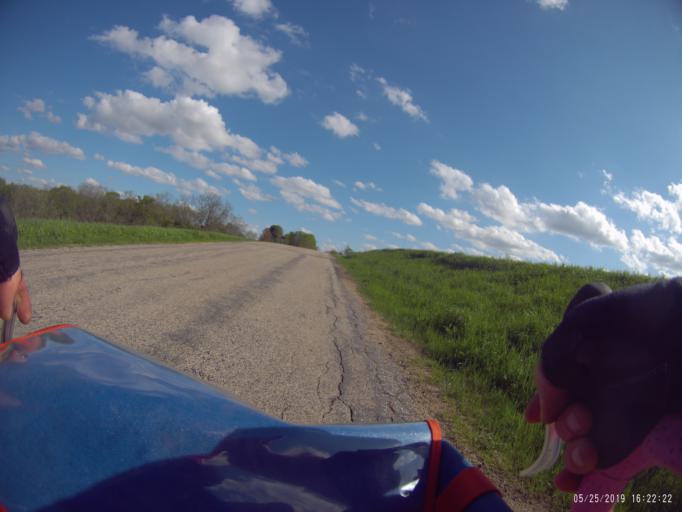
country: US
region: Wisconsin
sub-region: Dane County
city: Mount Horeb
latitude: 42.9618
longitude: -89.7014
